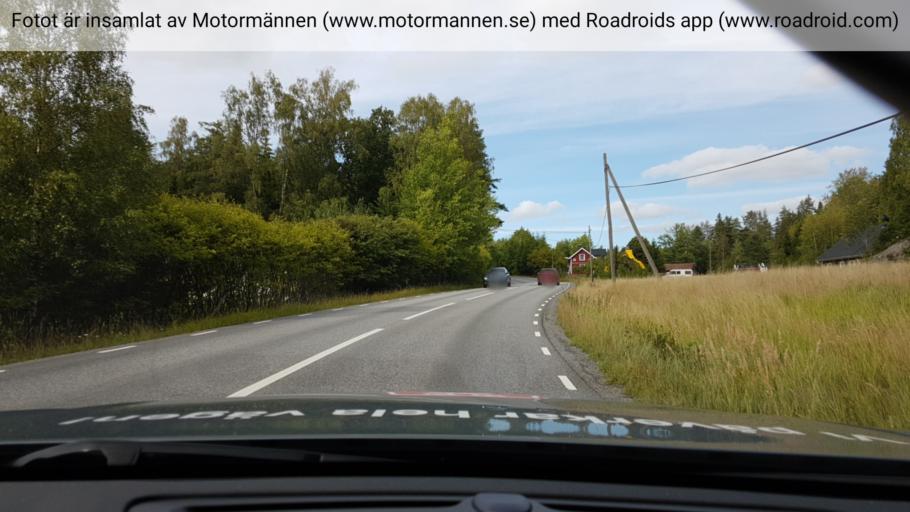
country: SE
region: Stockholm
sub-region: Haninge Kommun
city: Jordbro
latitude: 59.1211
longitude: 18.0115
